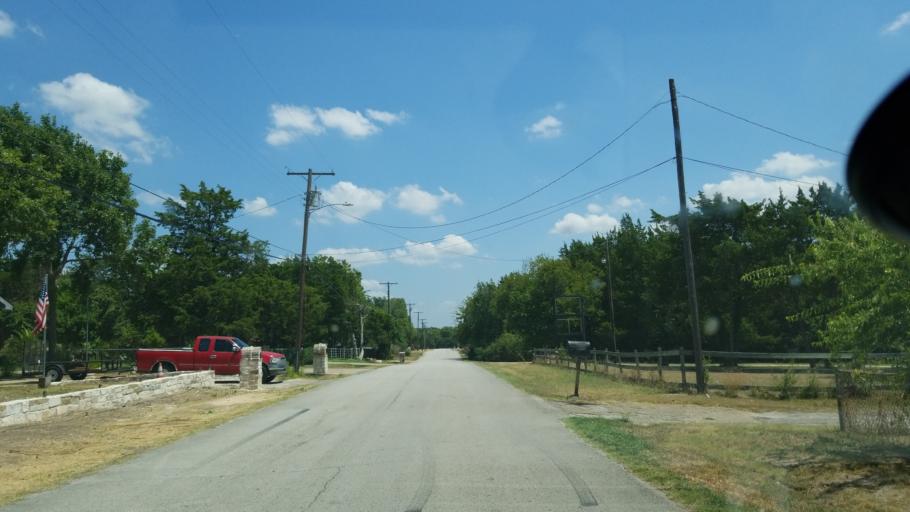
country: US
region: Texas
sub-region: Dallas County
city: Duncanville
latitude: 32.6719
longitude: -96.8951
